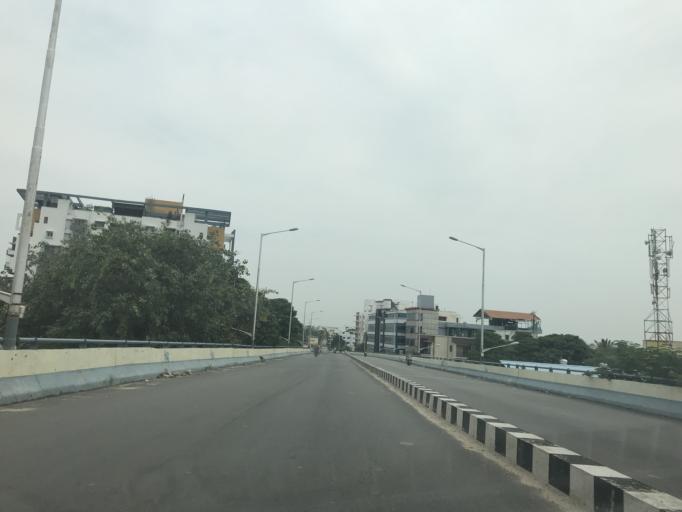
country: IN
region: Karnataka
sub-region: Bangalore Urban
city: Bangalore
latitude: 13.0264
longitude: 77.6319
